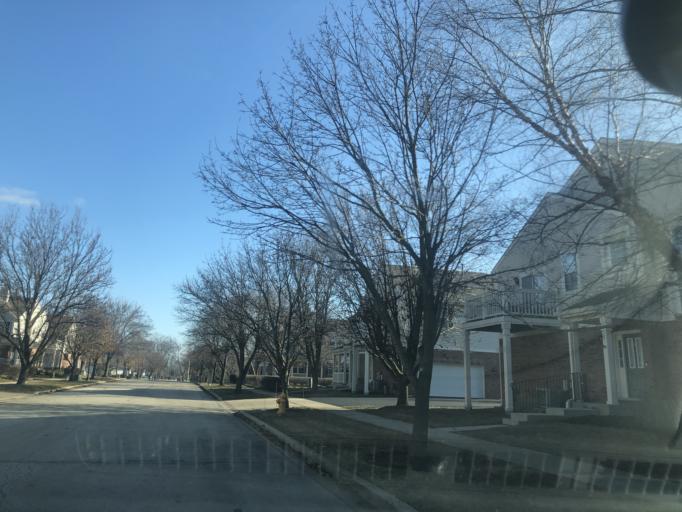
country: US
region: Illinois
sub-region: DuPage County
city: Addison
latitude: 41.9274
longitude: -88.0053
